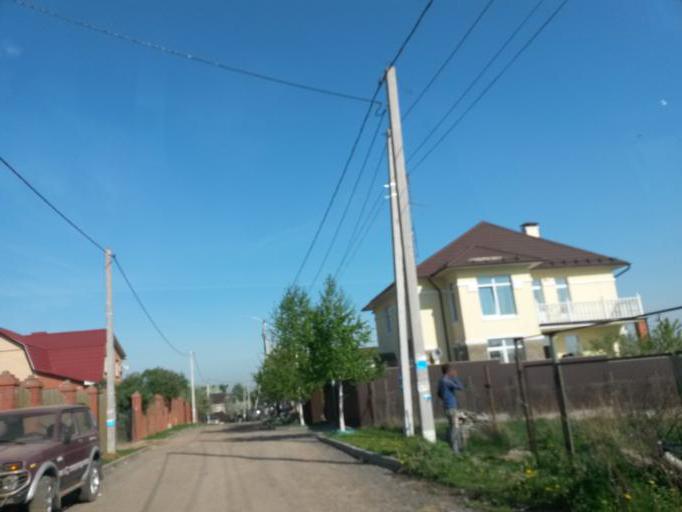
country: RU
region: Moskovskaya
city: Alekseyevka
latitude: 55.6099
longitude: 37.7908
